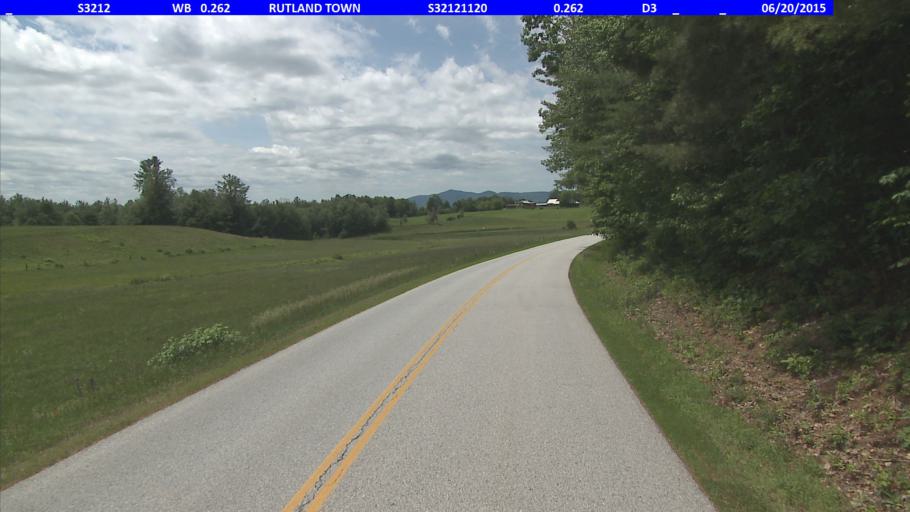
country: US
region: Vermont
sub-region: Rutland County
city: Rutland
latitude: 43.6444
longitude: -72.9419
